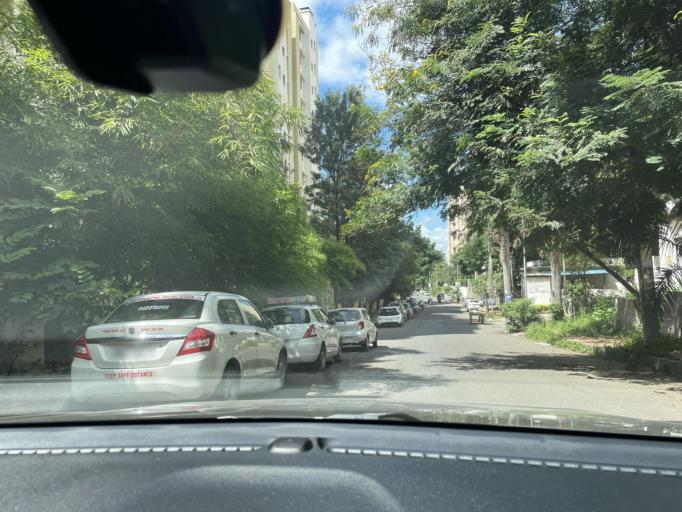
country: IN
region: Maharashtra
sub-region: Pune Division
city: Kharakvasla
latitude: 18.5123
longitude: 73.7772
